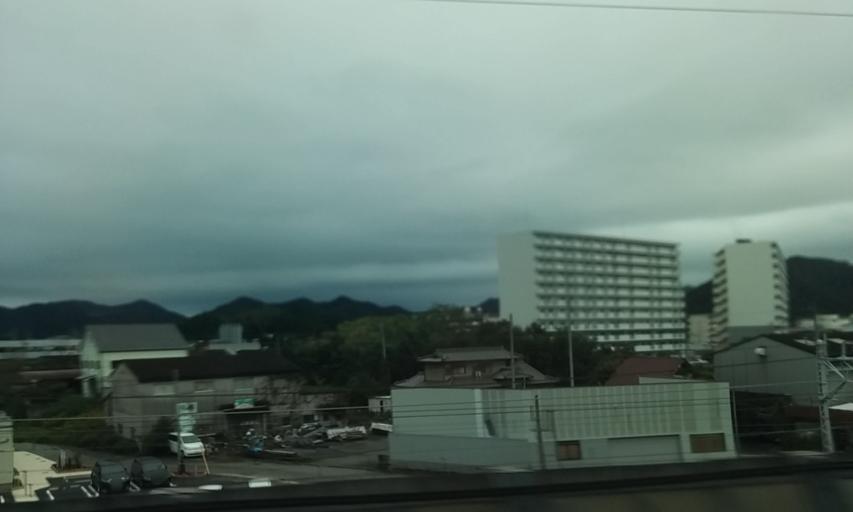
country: JP
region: Hyogo
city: Himeji
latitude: 34.8184
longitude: 134.7325
